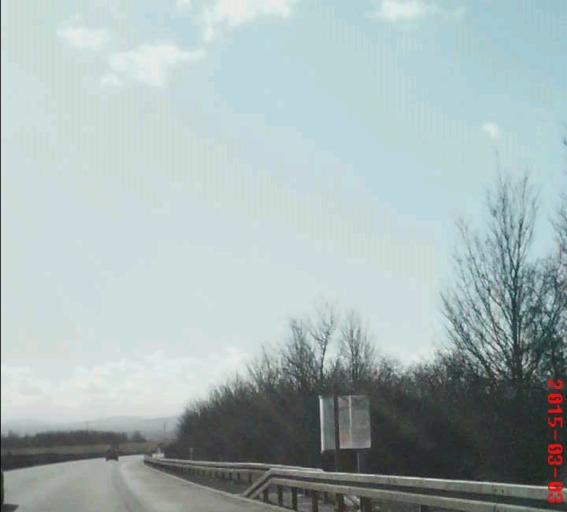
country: DE
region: Thuringia
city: Ingersleben
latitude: 50.9455
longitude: 10.9515
